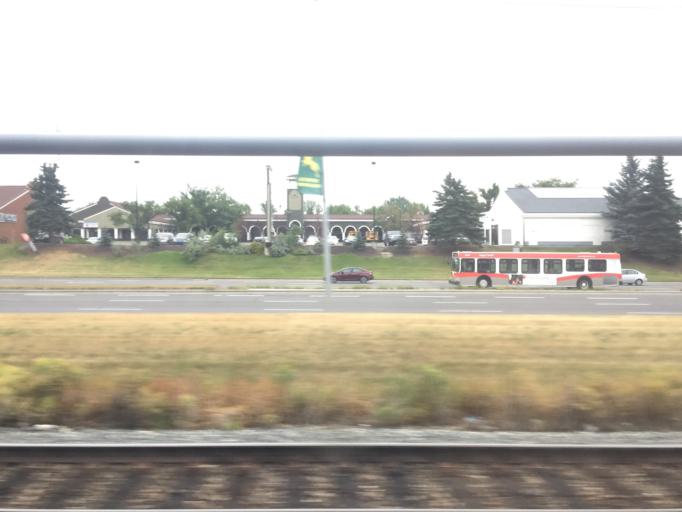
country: CA
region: Alberta
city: Calgary
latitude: 50.9409
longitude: -114.0703
